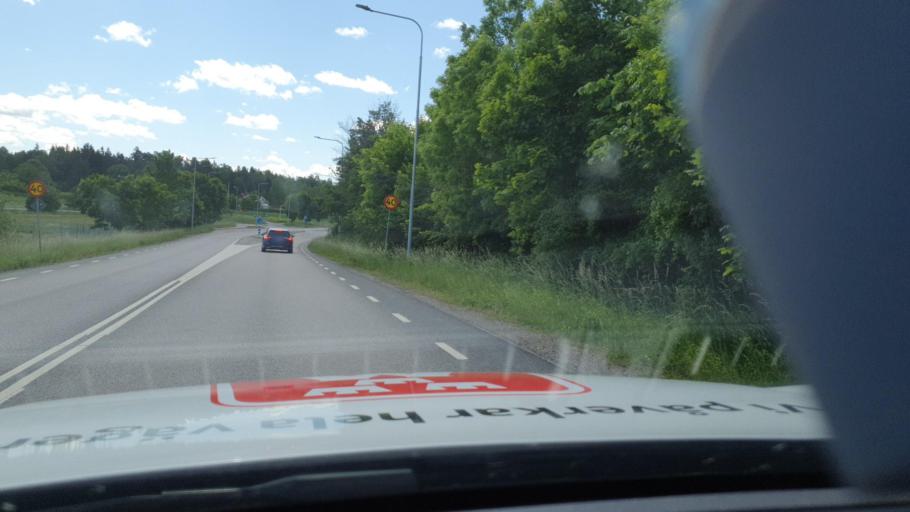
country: SE
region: Uppsala
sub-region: Knivsta Kommun
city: Knivsta
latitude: 59.7226
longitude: 17.7754
